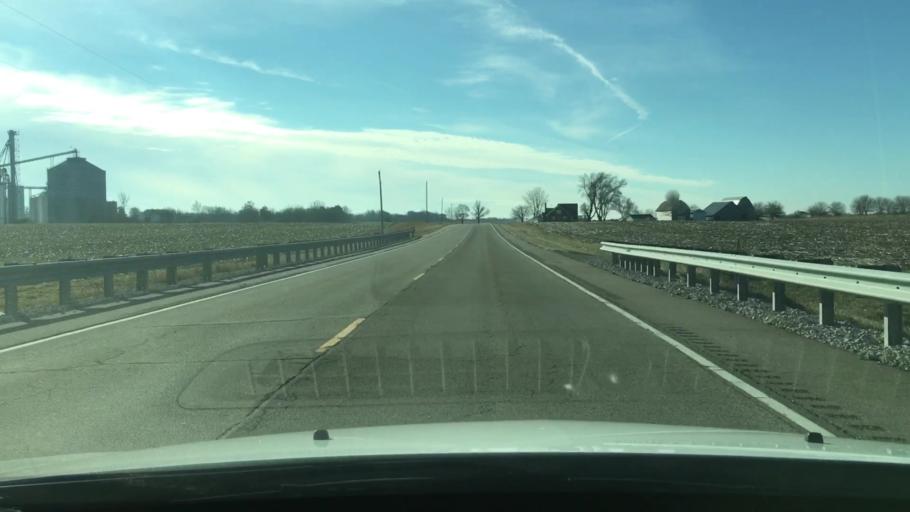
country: US
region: Illinois
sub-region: Woodford County
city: Washburn
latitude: 40.8798
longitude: -89.3168
